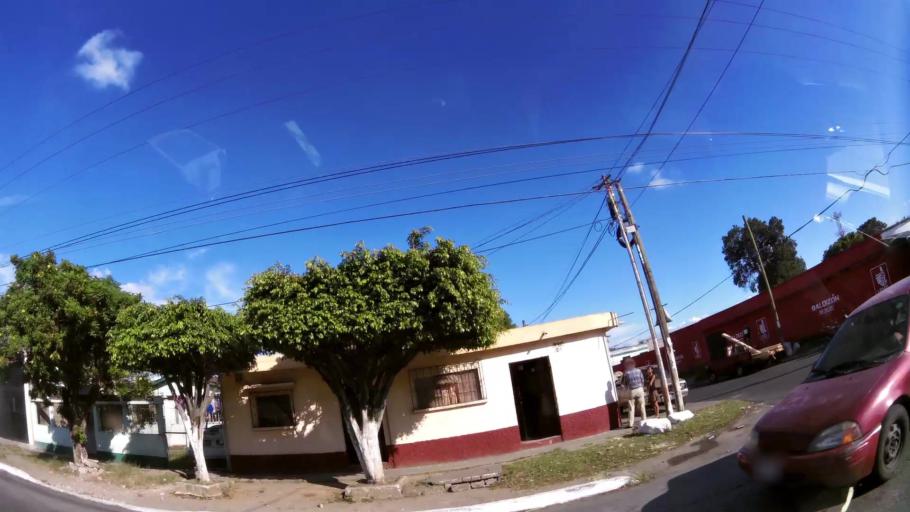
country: GT
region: Guatemala
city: Villa Nueva
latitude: 14.5168
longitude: -90.5737
